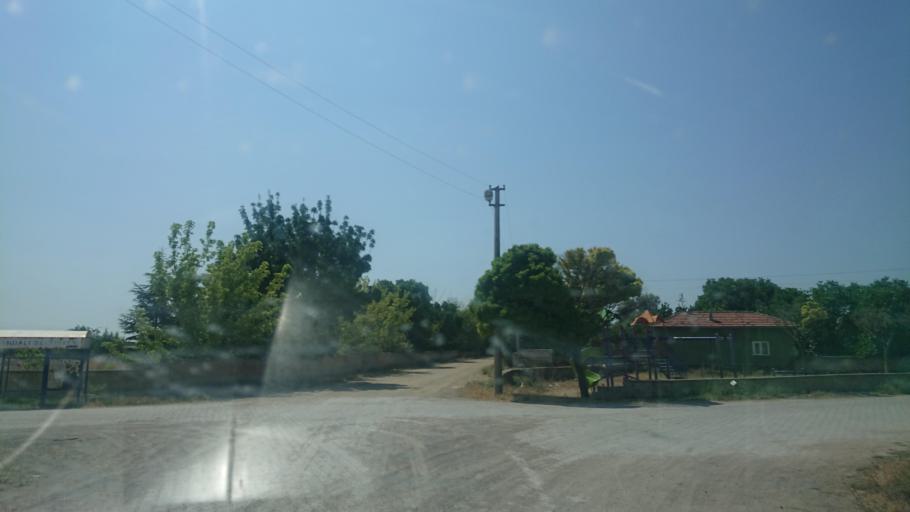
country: TR
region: Aksaray
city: Agacoren
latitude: 38.9305
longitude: 33.9600
